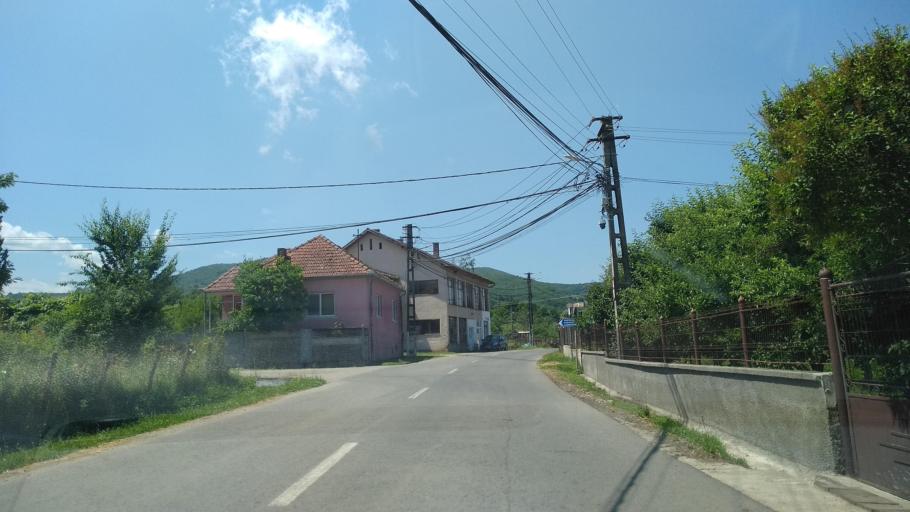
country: RO
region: Hunedoara
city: Densus
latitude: 45.5789
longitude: 22.8064
